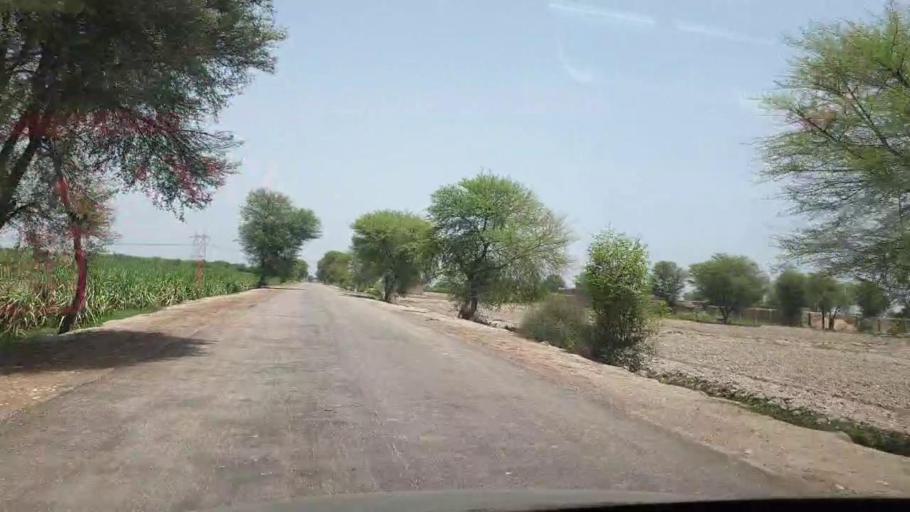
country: PK
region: Sindh
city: Daulatpur
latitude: 26.3894
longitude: 68.0766
